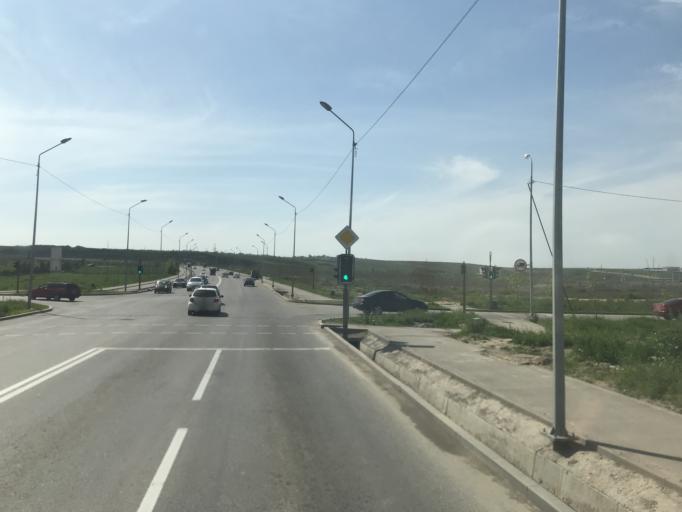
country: KZ
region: Almaty Oblysy
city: Burunday
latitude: 43.3136
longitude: 76.8428
